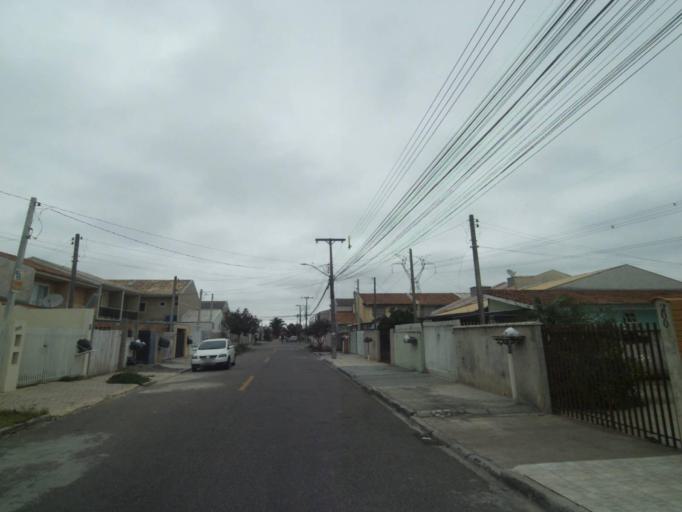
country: BR
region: Parana
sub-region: Araucaria
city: Araucaria
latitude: -25.5451
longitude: -49.3432
